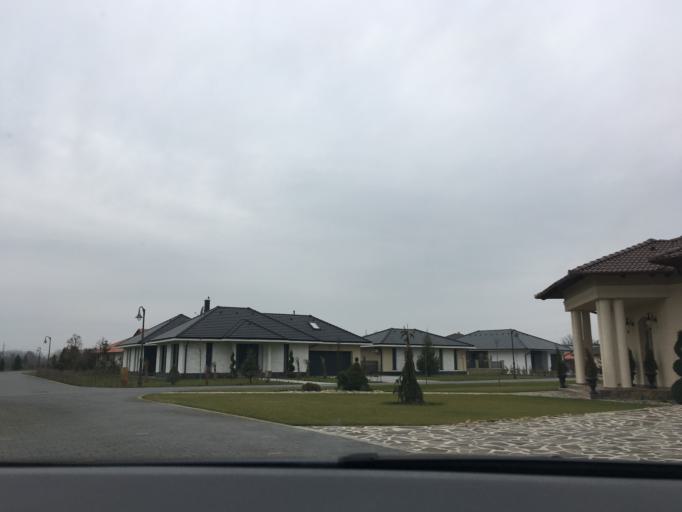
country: HU
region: Hajdu-Bihar
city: Debrecen
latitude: 47.5515
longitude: 21.6900
